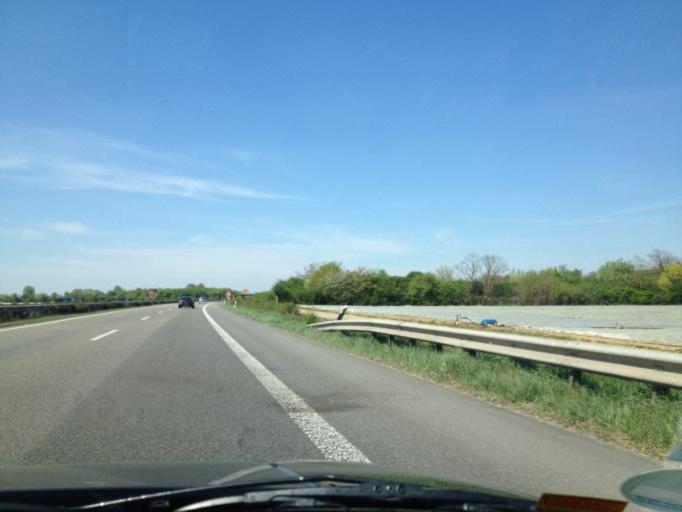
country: DE
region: Rheinland-Pfalz
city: Mutterstadt
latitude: 49.4437
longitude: 8.3738
